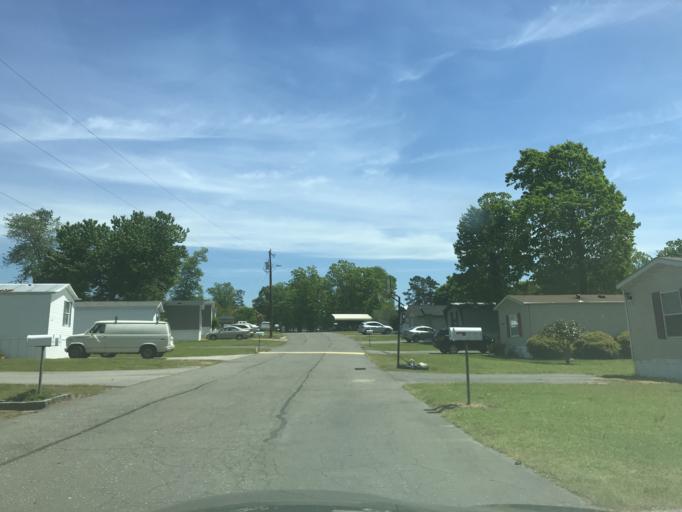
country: US
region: North Carolina
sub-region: Wake County
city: Raleigh
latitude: 35.8251
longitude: -78.5755
